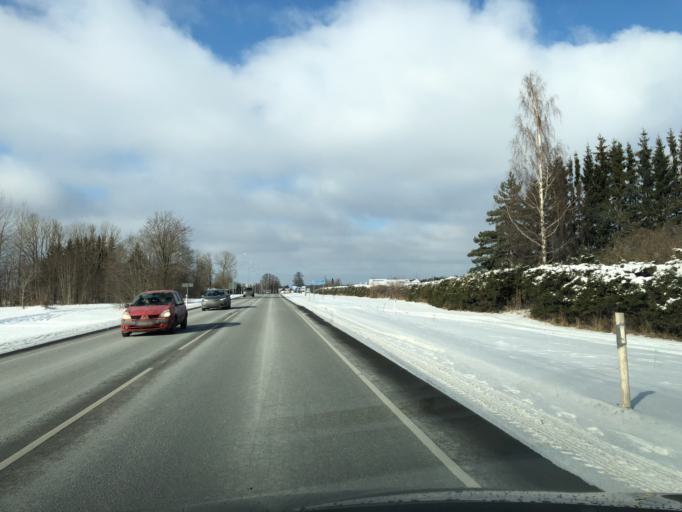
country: EE
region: Jaervamaa
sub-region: Paide linn
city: Paide
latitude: 58.8759
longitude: 25.6968
